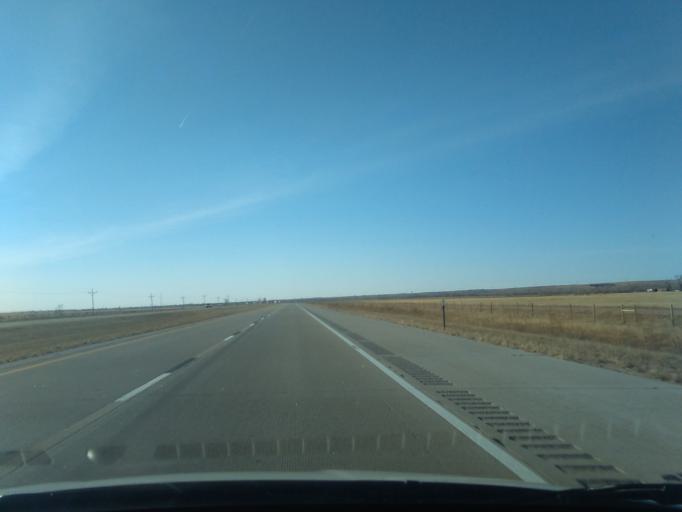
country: US
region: Colorado
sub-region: Sedgwick County
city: Julesburg
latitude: 41.0626
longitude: -101.9999
